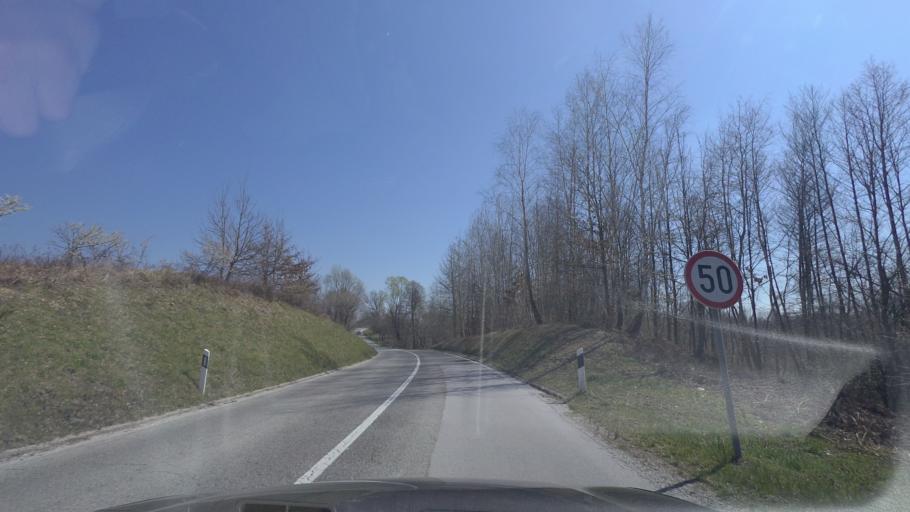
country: HR
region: Sisacko-Moslavacka
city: Gvozd
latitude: 45.3399
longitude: 15.8970
